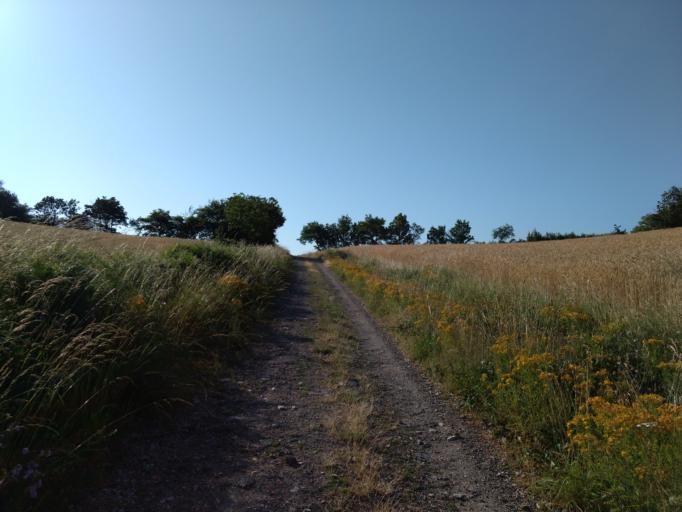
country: FR
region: Midi-Pyrenees
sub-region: Departement de l'Aveyron
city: La Loubiere
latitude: 44.3619
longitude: 2.7041
